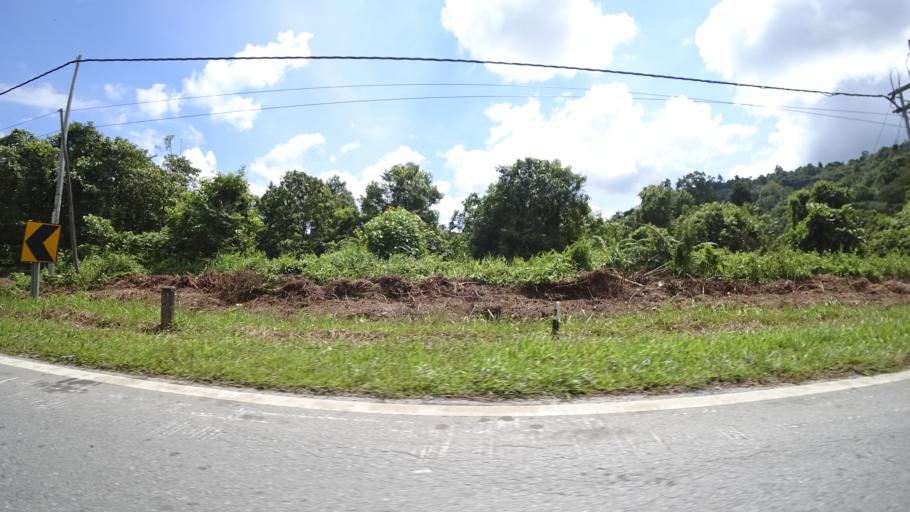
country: MY
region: Sarawak
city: Limbang
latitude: 4.6646
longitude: 114.9801
